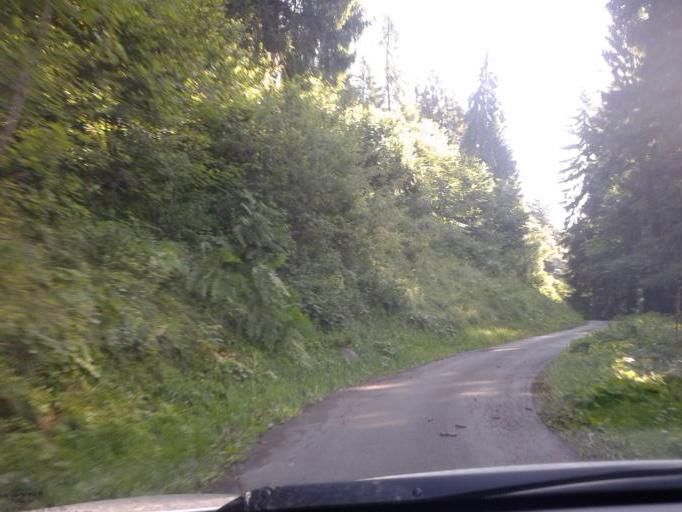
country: IT
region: Trentino-Alto Adige
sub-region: Provincia di Trento
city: Storo
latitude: 45.8665
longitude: 10.5515
